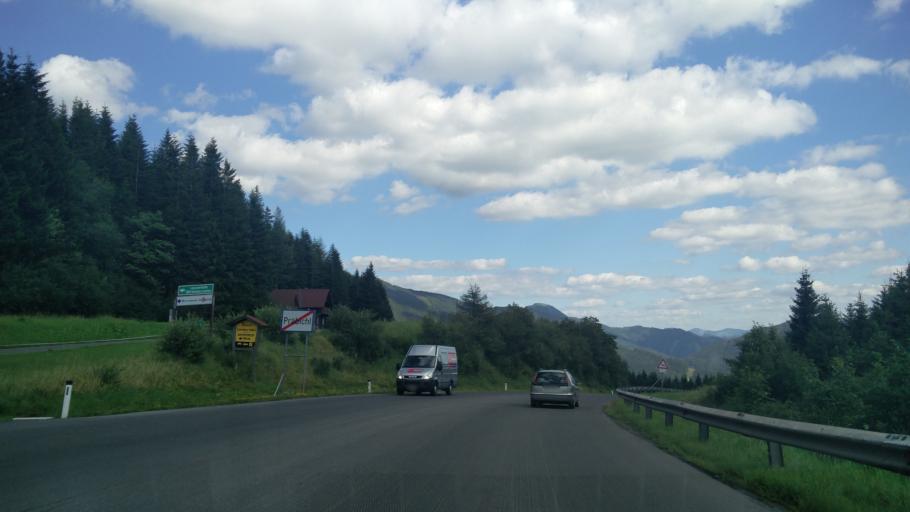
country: AT
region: Styria
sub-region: Politischer Bezirk Leoben
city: Vordernberg
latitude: 47.5213
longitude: 14.9541
